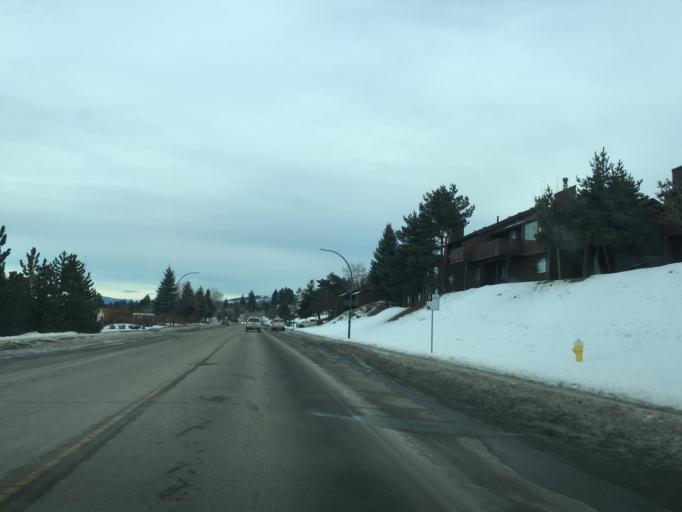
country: CA
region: British Columbia
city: Kamloops
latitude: 50.6488
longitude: -120.3701
